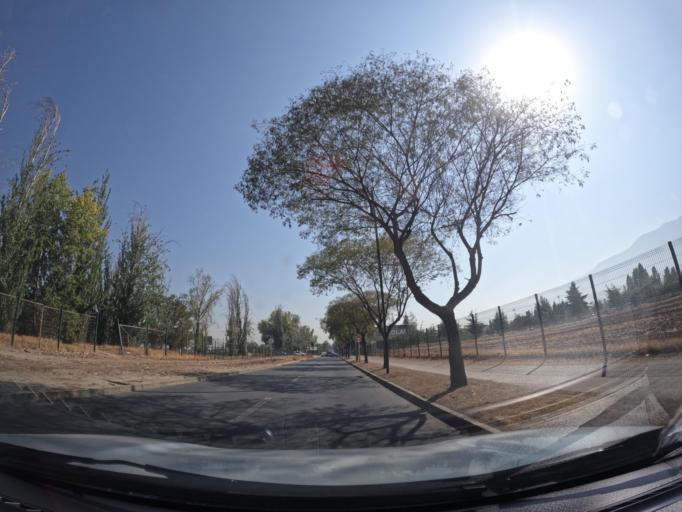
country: CL
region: Santiago Metropolitan
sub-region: Provincia de Santiago
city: Villa Presidente Frei, Nunoa, Santiago, Chile
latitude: -33.4929
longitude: -70.5586
